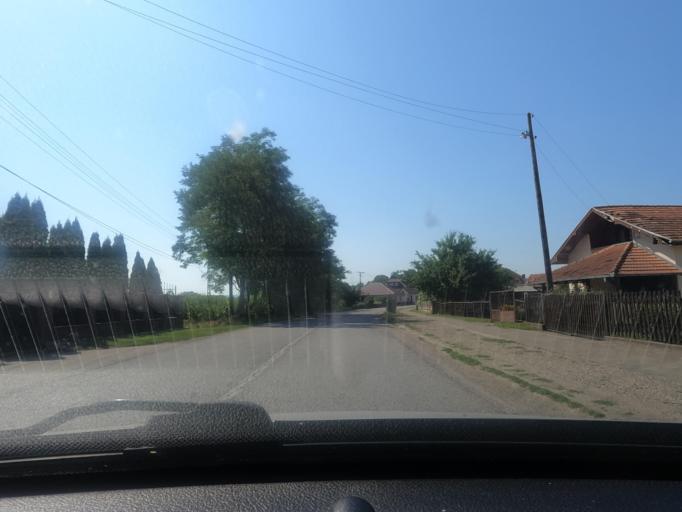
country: RS
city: Lipnicki Sor
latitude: 44.5813
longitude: 19.2596
